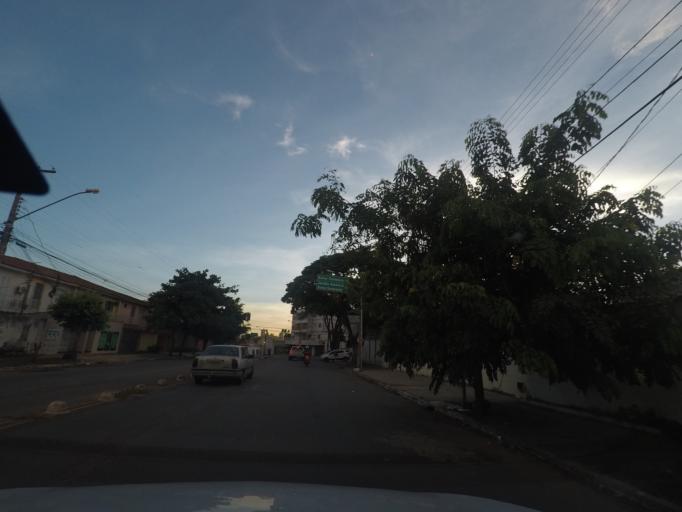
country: BR
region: Goias
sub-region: Goiania
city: Goiania
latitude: -16.6907
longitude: -49.2843
